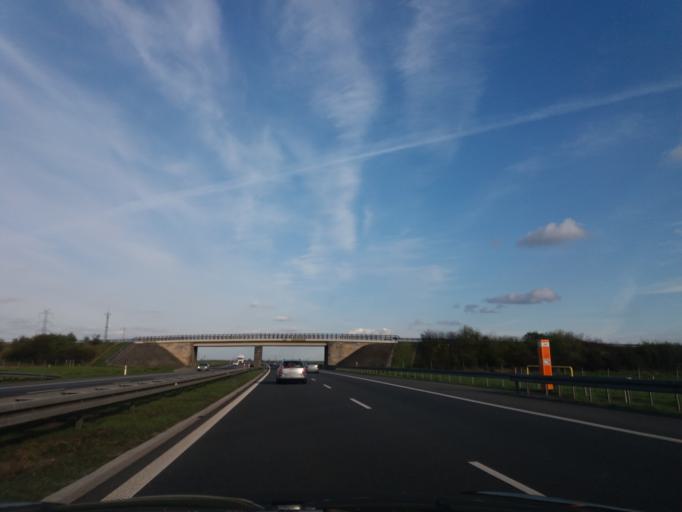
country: PL
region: Opole Voivodeship
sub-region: Powiat brzeski
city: Olszanka
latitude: 50.7386
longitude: 17.4691
